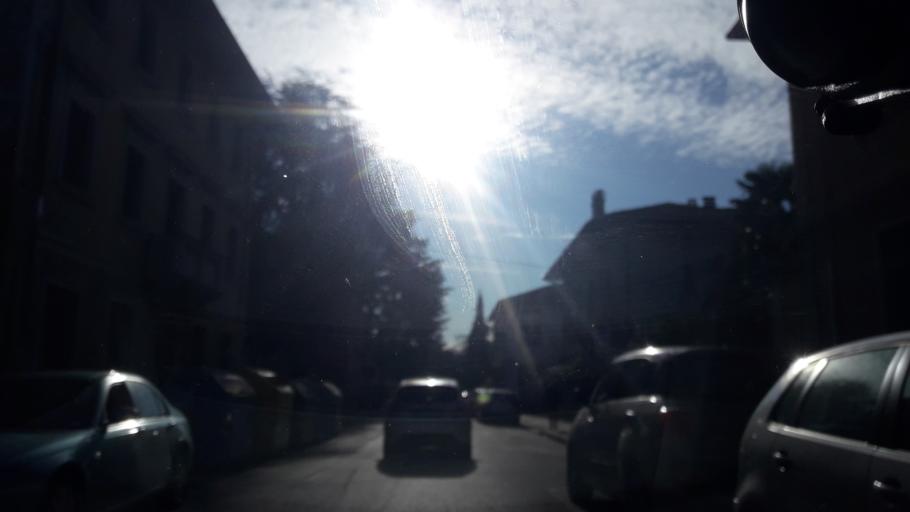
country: IT
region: Friuli Venezia Giulia
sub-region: Provincia di Udine
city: Udine
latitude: 46.0735
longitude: 13.2308
